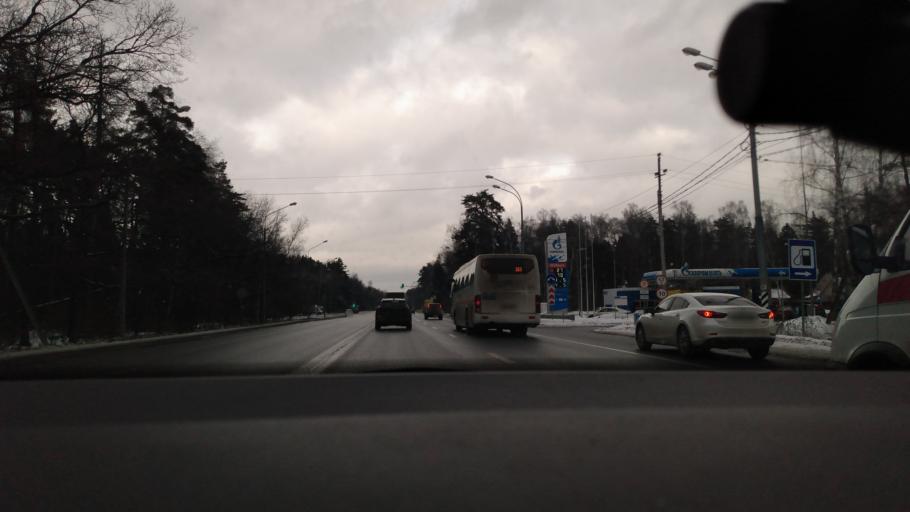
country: RU
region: Moskovskaya
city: Medvezh'i Ozera
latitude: 55.8792
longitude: 38.0018
